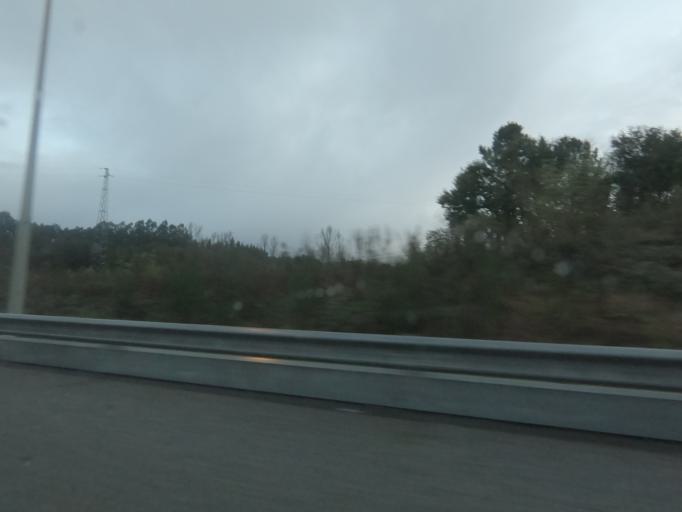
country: PT
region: Braga
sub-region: Braga
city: Oliveira
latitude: 41.5359
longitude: -8.4955
